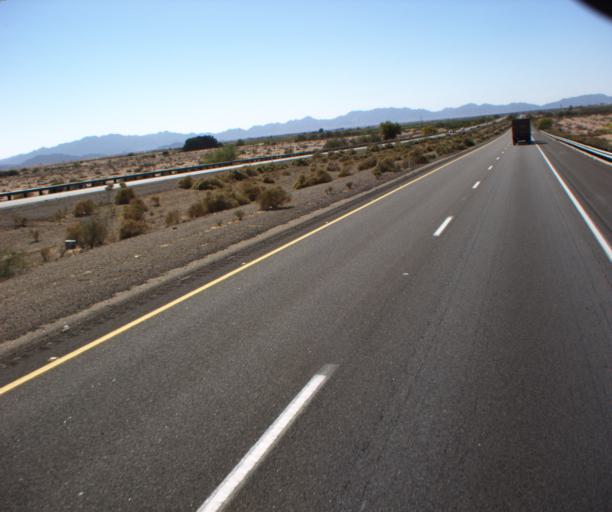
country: US
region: Arizona
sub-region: Yuma County
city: Wellton
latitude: 32.6764
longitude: -114.0507
